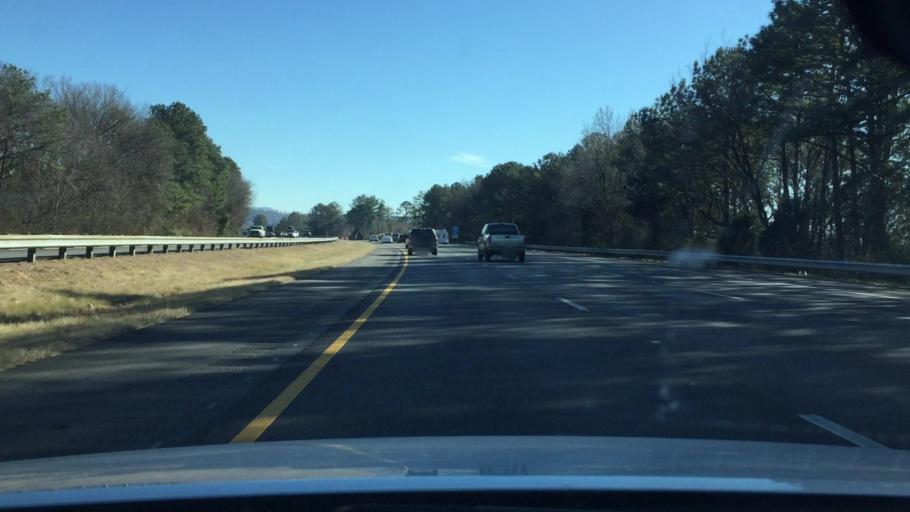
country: US
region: Georgia
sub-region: Catoosa County
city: Ringgold
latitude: 34.9164
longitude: -85.1453
